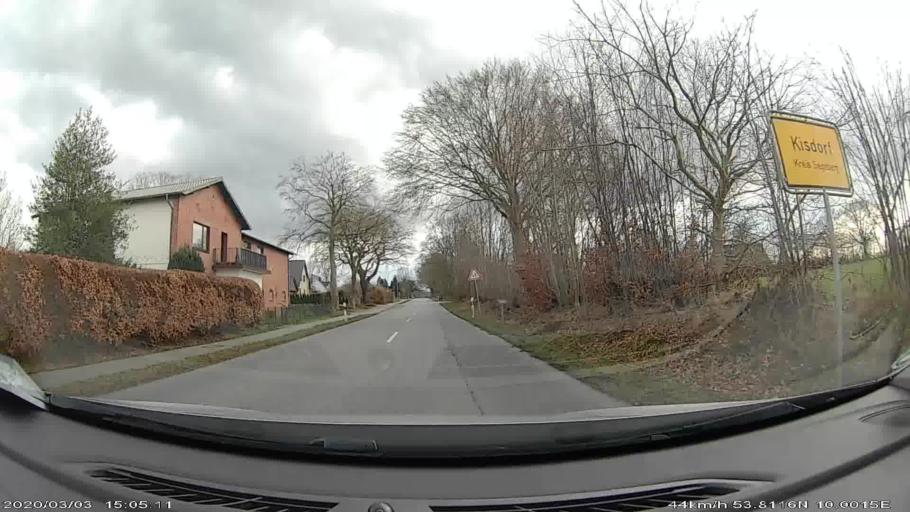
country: DE
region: Schleswig-Holstein
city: Kisdorf
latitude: 53.8118
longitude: 10.0014
